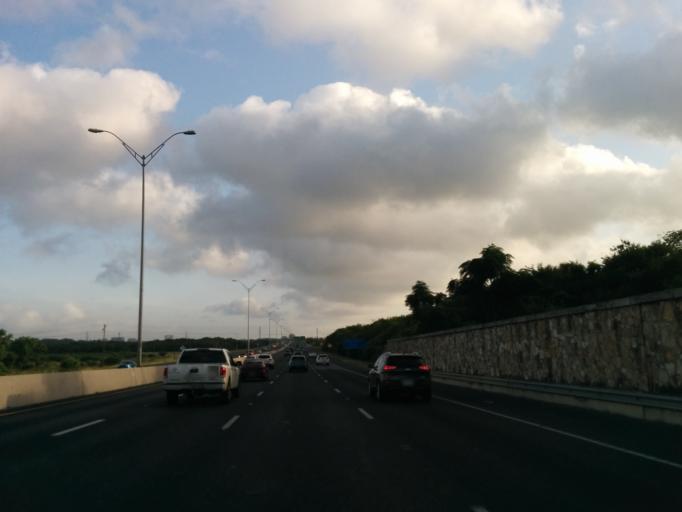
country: US
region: Texas
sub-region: Bexar County
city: Olmos Park
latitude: 29.4833
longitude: -98.4820
